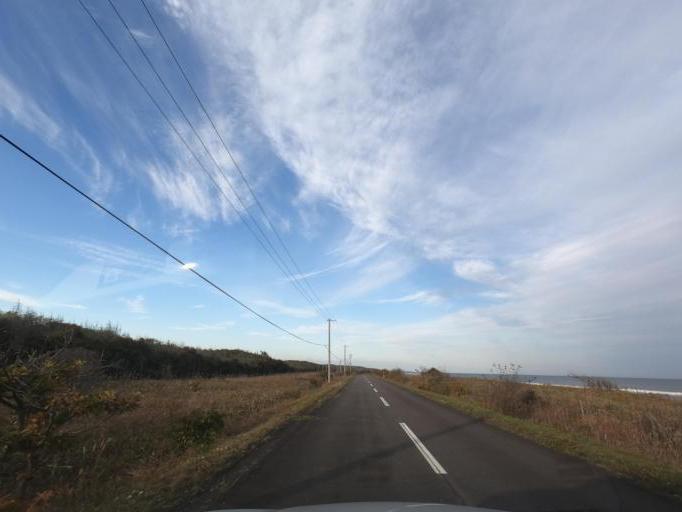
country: JP
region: Hokkaido
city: Obihiro
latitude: 42.5397
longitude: 143.4900
